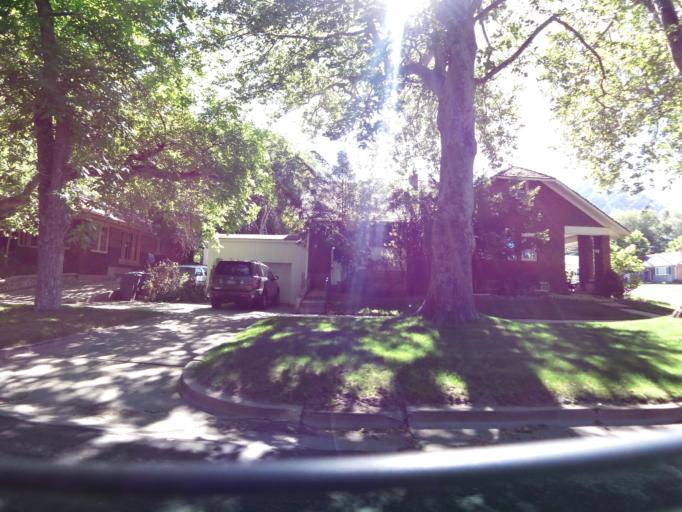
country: US
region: Utah
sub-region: Weber County
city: Ogden
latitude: 41.2216
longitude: -111.9426
